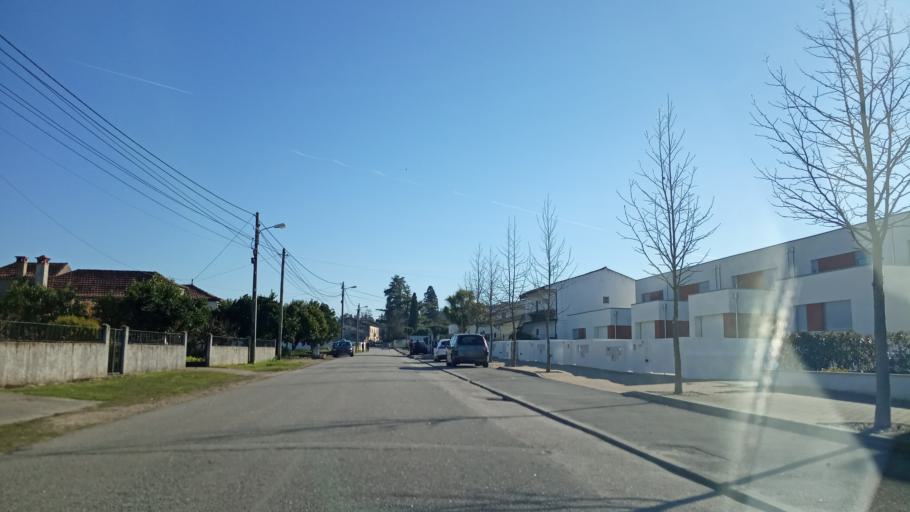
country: PT
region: Aveiro
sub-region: Anadia
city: Anadia
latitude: 40.4299
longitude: -8.4293
